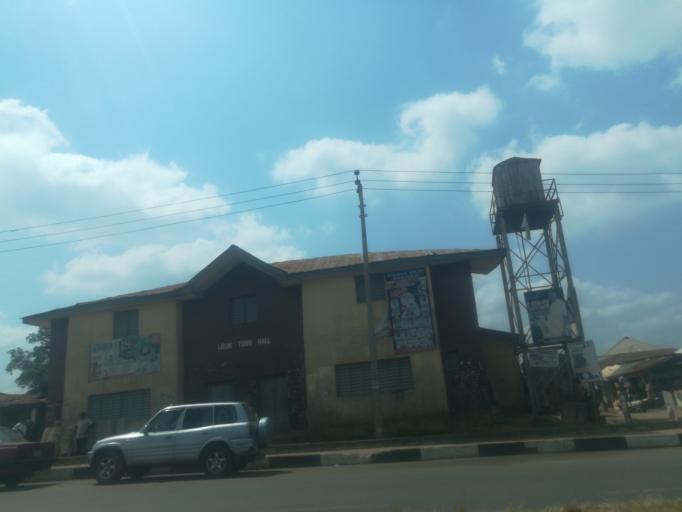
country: NG
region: Ogun
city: Abeokuta
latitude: 7.1523
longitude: 3.3510
